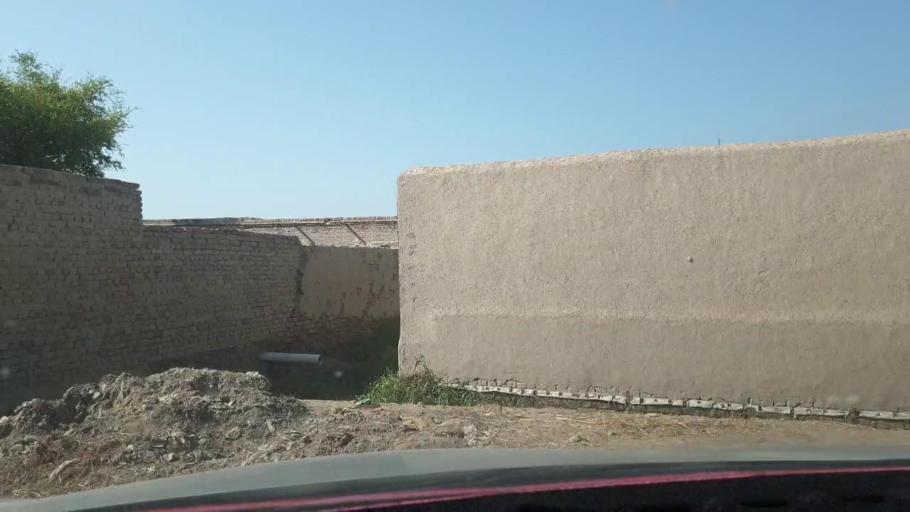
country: PK
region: Sindh
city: Nasirabad
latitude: 27.3852
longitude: 67.8724
